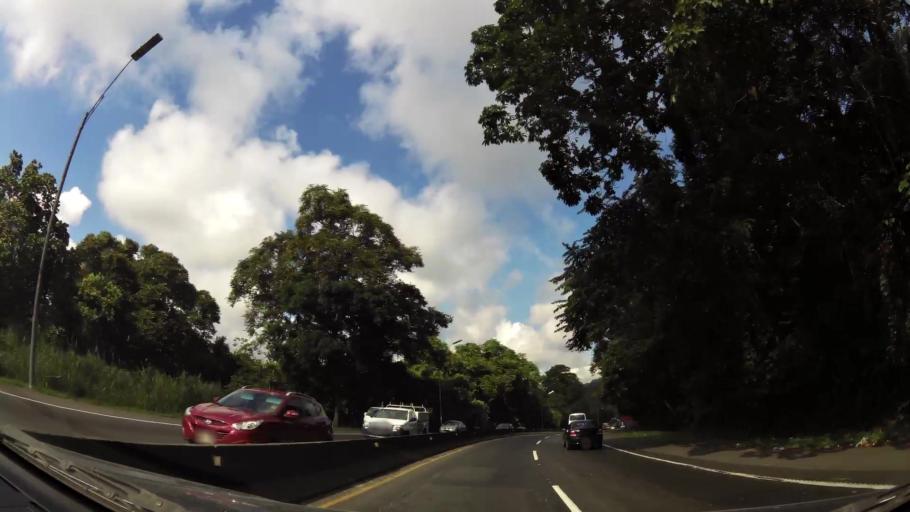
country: PA
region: Panama
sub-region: Distrito de Panama
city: Ancon
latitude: 8.9540
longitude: -79.5944
